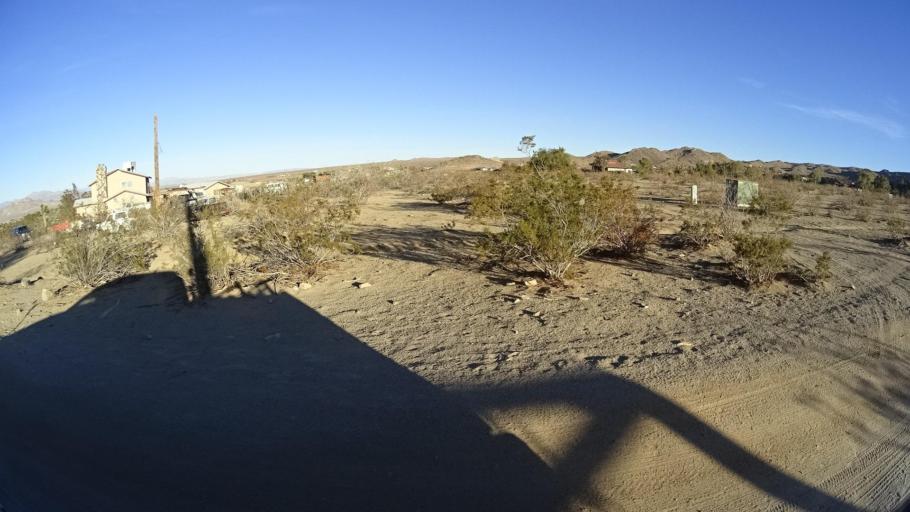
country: US
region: California
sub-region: Kern County
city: Ridgecrest
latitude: 35.5834
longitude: -117.6614
